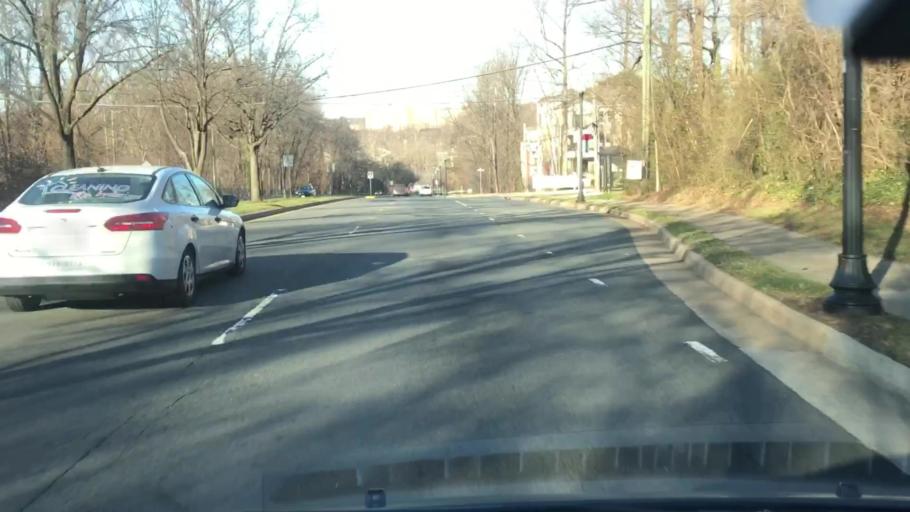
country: US
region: Virginia
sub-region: Fairfax County
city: Mantua
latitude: 38.8573
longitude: -77.2707
